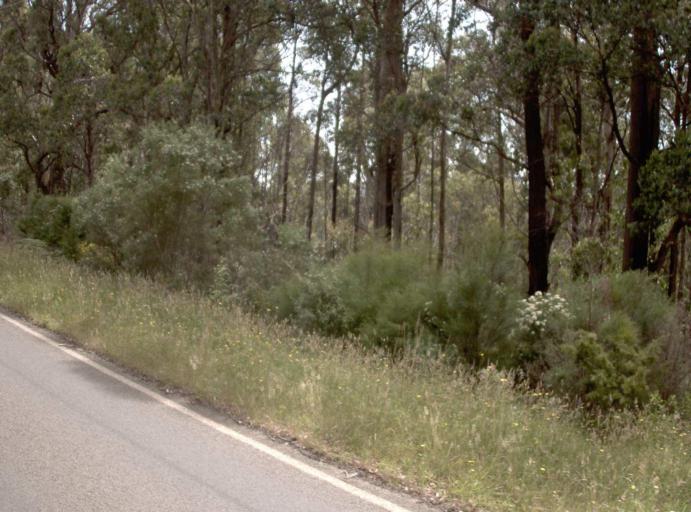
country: AU
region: Victoria
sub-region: Latrobe
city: Moe
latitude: -37.9349
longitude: 146.4025
